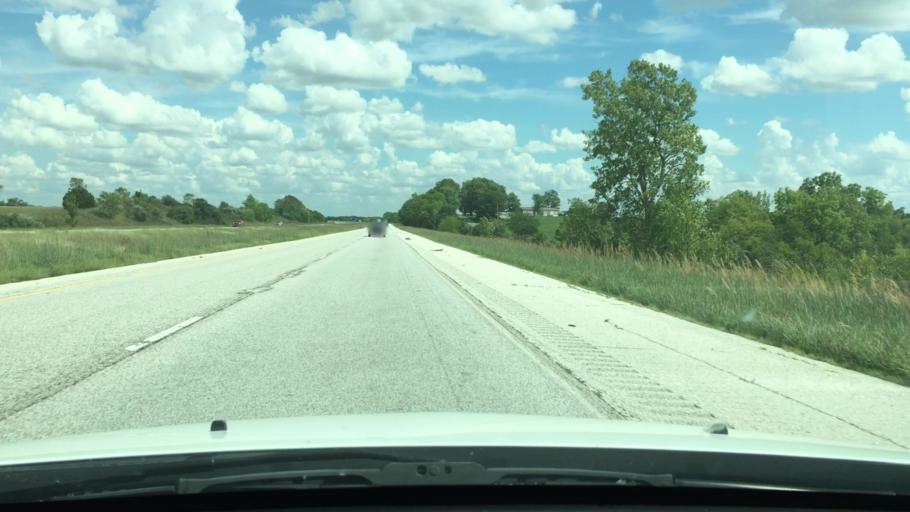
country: US
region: Illinois
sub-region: Morgan County
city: South Jacksonville
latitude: 39.6803
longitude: -90.2785
